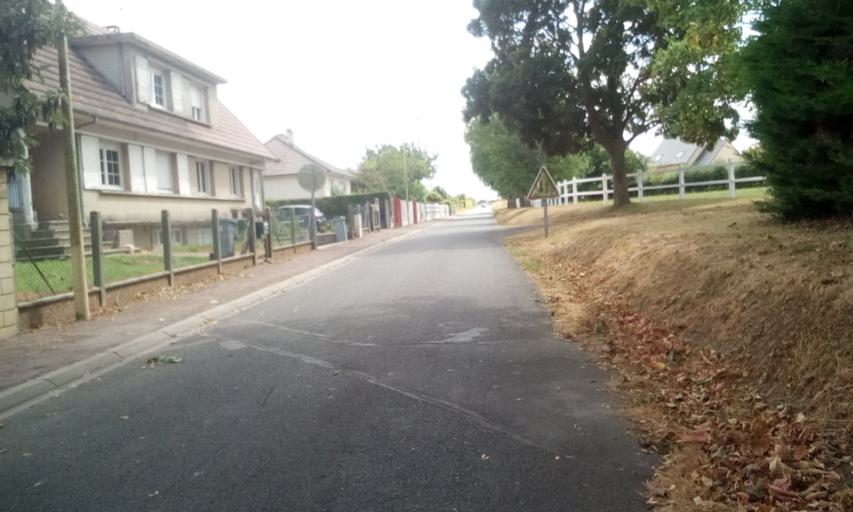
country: FR
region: Lower Normandy
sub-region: Departement du Calvados
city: Creully
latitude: 49.2840
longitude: -0.5366
